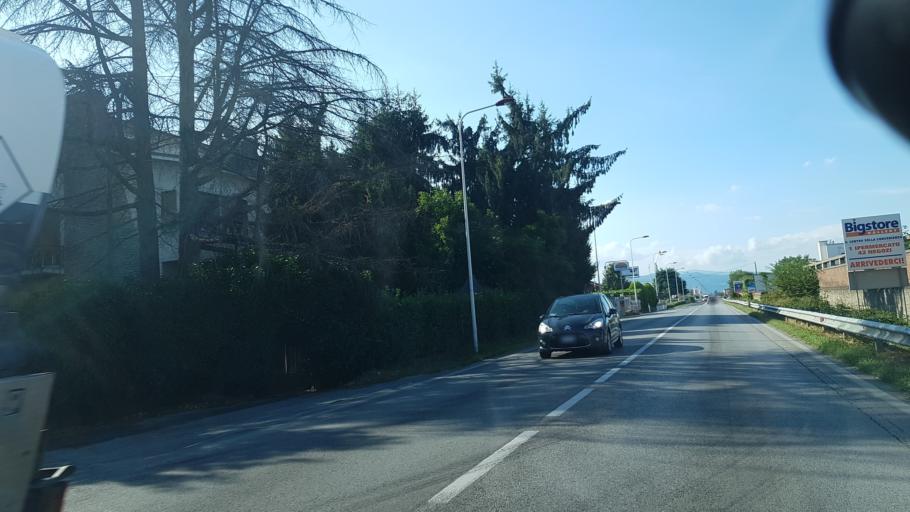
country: IT
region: Piedmont
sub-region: Provincia di Cuneo
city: Roata Rossi
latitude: 44.4210
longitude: 7.5455
